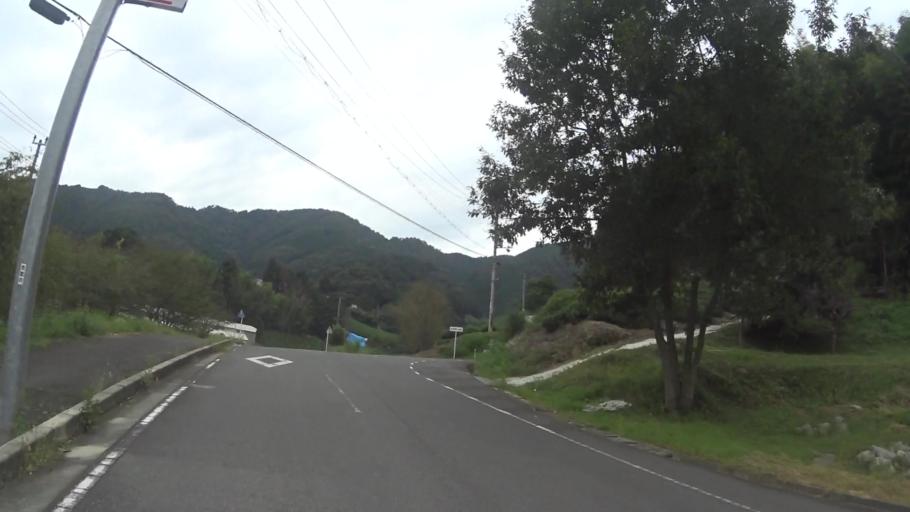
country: JP
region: Kyoto
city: Tanabe
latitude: 34.7947
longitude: 135.8874
